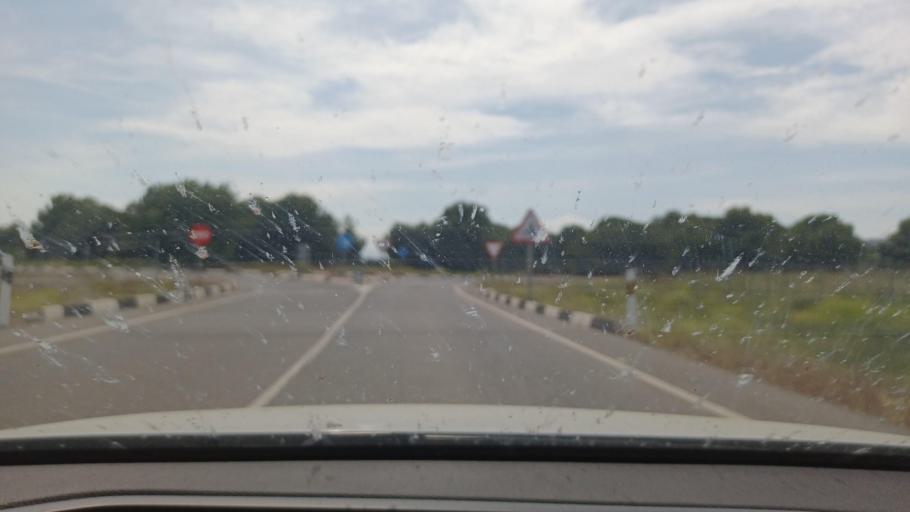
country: ES
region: Valencia
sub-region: Provincia de Castello
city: Castello de la Plana
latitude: 40.0265
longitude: -0.0011
